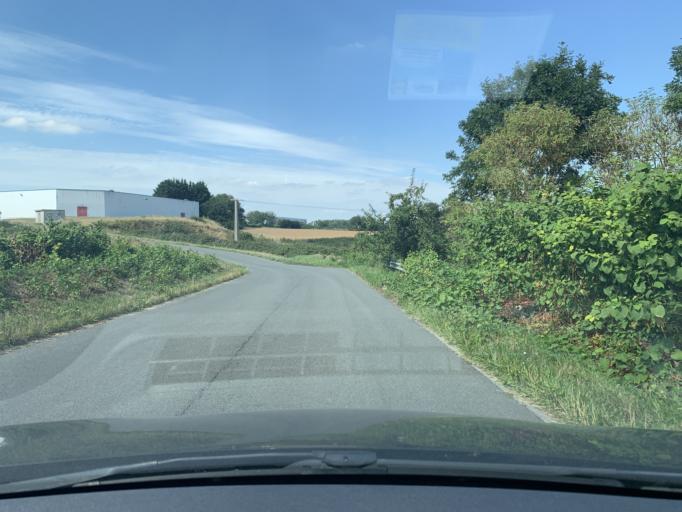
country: FR
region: Nord-Pas-de-Calais
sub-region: Departement du Nord
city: Cambrai
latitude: 50.1499
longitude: 3.2228
